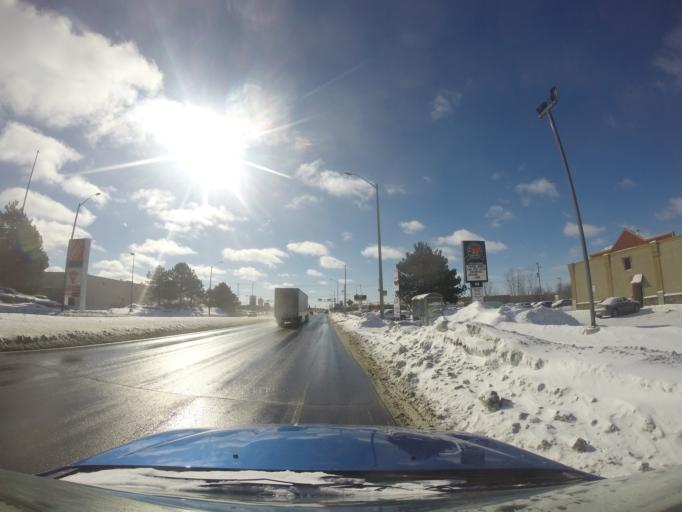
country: CA
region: Ontario
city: Cambridge
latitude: 43.4068
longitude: -80.3279
